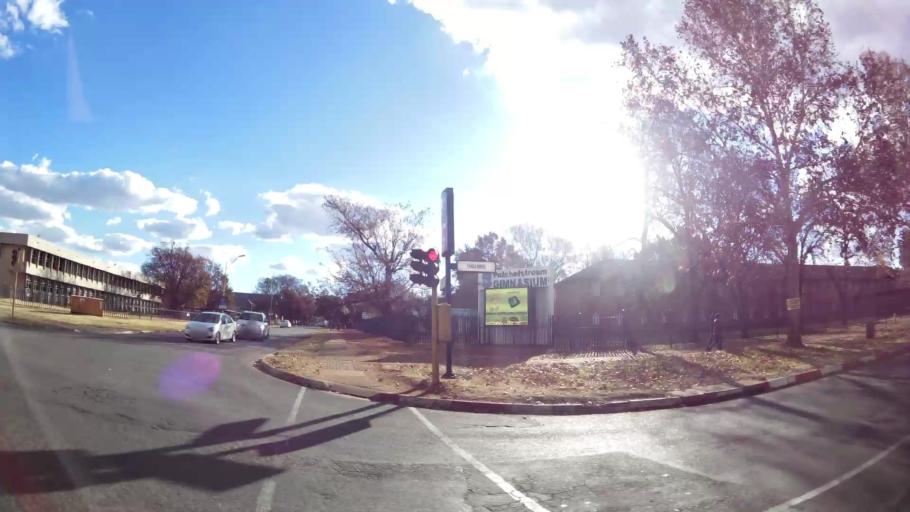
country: ZA
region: North-West
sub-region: Dr Kenneth Kaunda District Municipality
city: Potchefstroom
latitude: -26.6914
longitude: 27.0978
